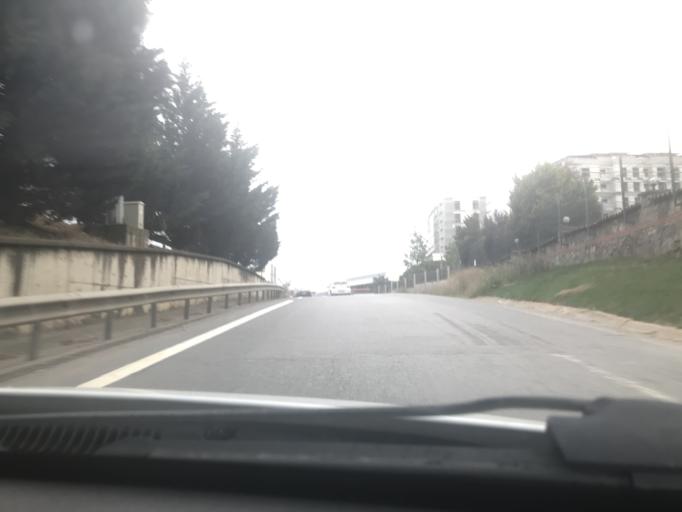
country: TR
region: Istanbul
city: Sultanbeyli
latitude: 40.9309
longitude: 29.3284
